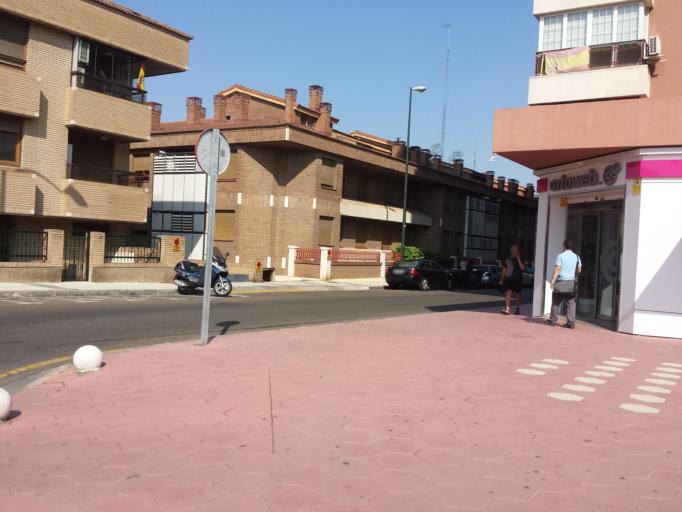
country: ES
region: Aragon
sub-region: Provincia de Zaragoza
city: Delicias
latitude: 41.6359
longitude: -0.8924
